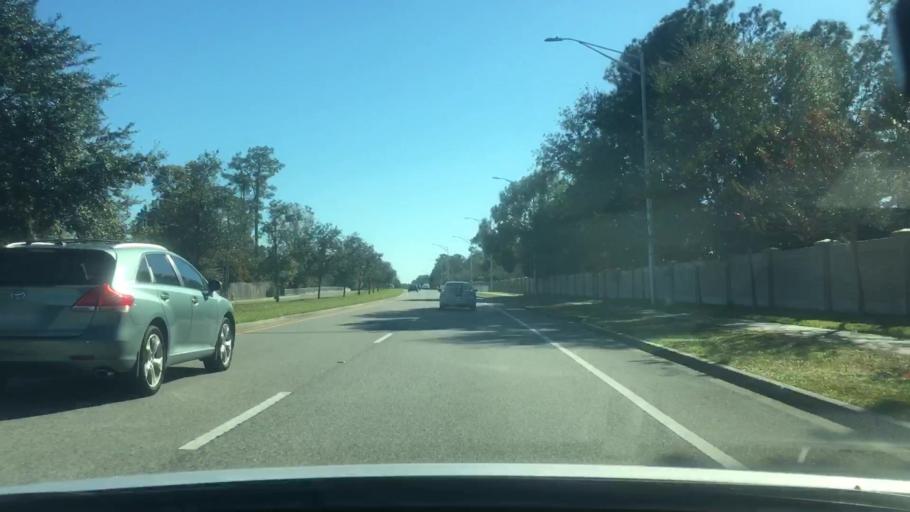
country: US
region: Florida
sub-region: Duval County
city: Neptune Beach
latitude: 30.3089
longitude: -81.4593
